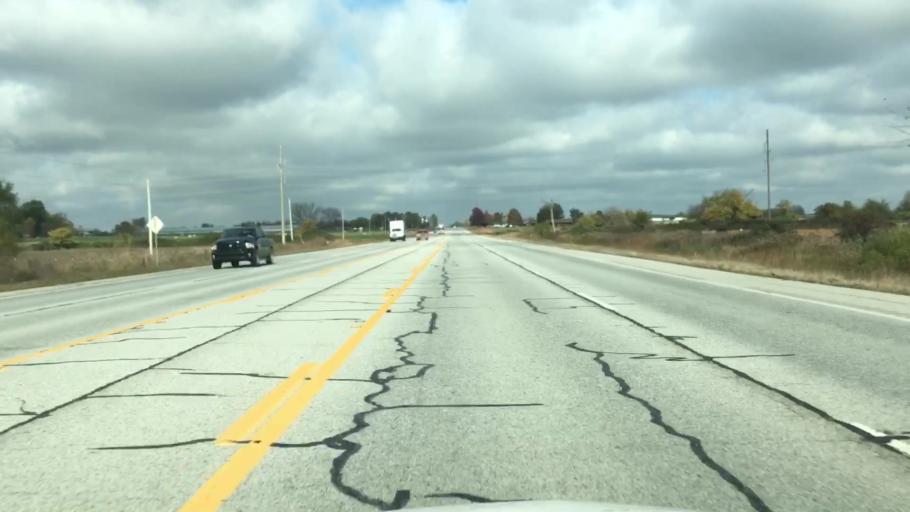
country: US
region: Arkansas
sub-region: Benton County
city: Siloam Springs
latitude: 36.2117
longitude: -94.4956
